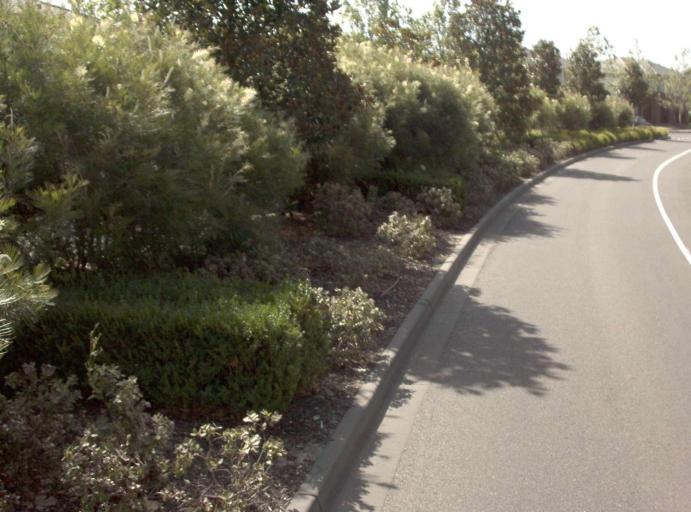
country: AU
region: Victoria
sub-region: Monash
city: Mulgrave
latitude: -37.9234
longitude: 145.1863
